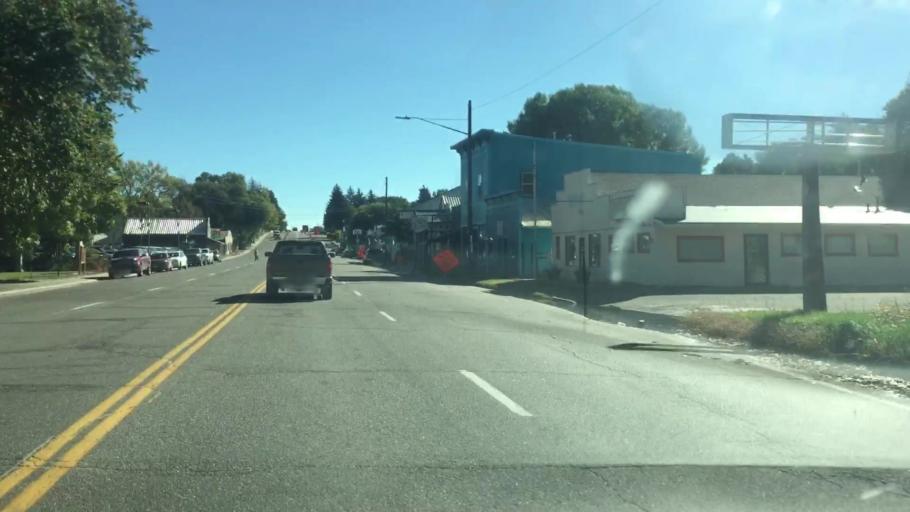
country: US
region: Colorado
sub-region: Elbert County
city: Kiowa
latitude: 39.3466
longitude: -104.4678
